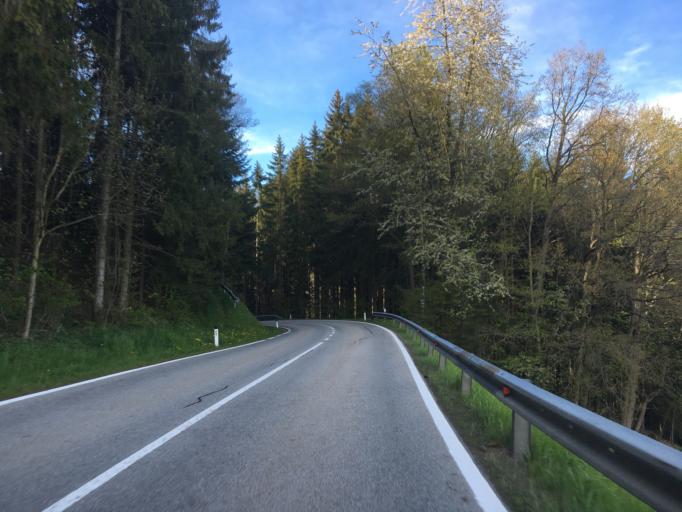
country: AT
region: Upper Austria
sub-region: Politischer Bezirk Urfahr-Umgebung
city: Haibach im Muhlkreis
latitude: 48.4375
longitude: 14.3573
